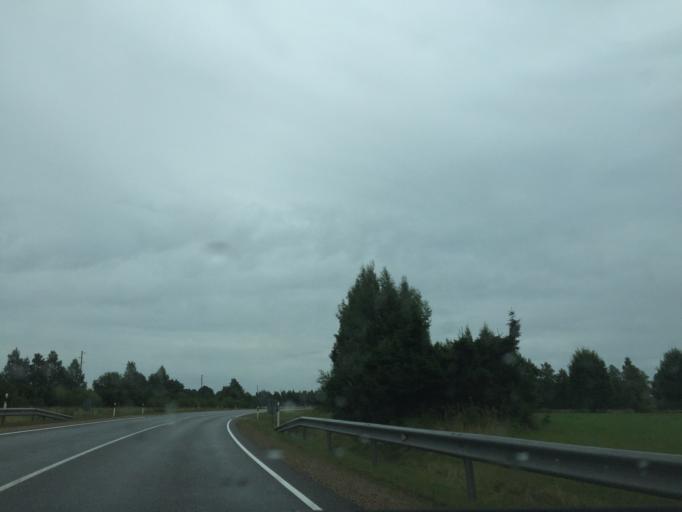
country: LV
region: Livani
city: Livani
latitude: 56.3989
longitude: 26.1359
